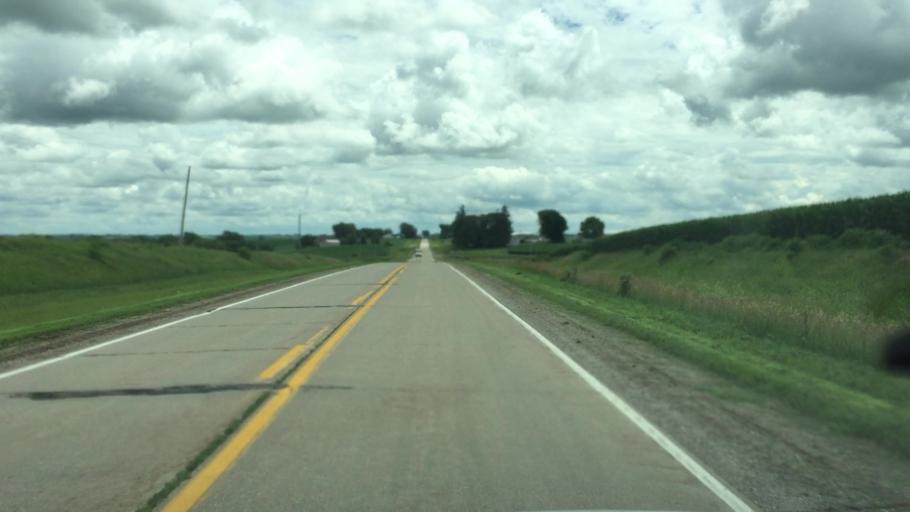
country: US
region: Iowa
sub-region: Jasper County
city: Monroe
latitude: 41.5807
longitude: -93.1255
